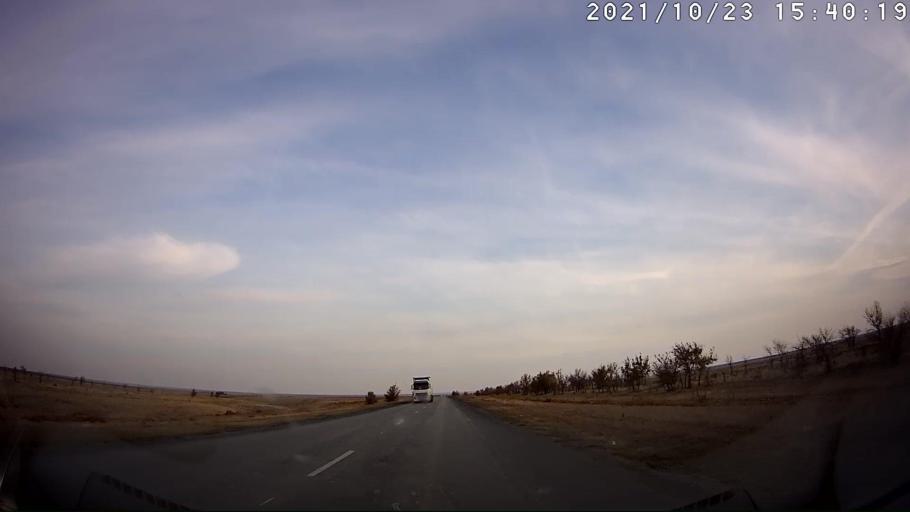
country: RU
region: Kalmykiya
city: Sadovoye
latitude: 48.1141
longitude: 44.1404
